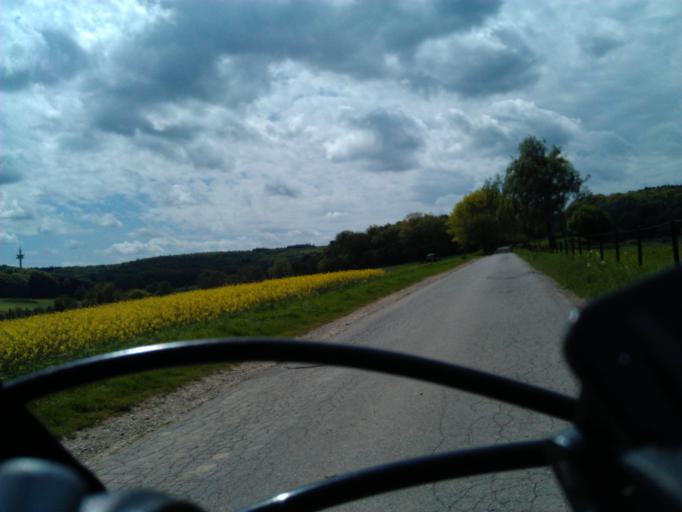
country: NL
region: Limburg
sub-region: Gemeente Vaals
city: Vaals
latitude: 50.7654
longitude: 6.0361
